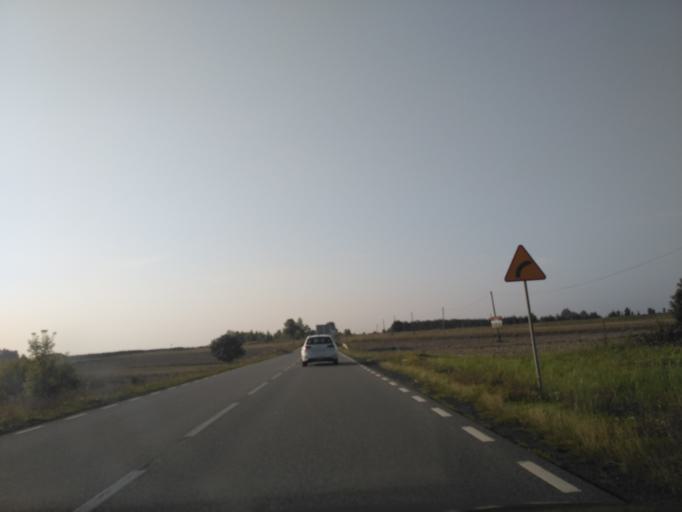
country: PL
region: Lublin Voivodeship
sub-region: Powiat janowski
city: Modliborzyce
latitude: 50.7855
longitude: 22.3212
